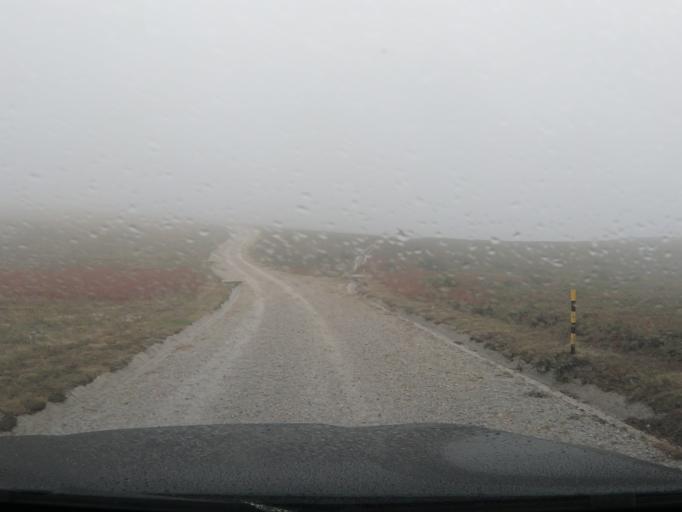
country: PT
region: Vila Real
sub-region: Vila Real
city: Vila Real
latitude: 41.3233
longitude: -7.8333
